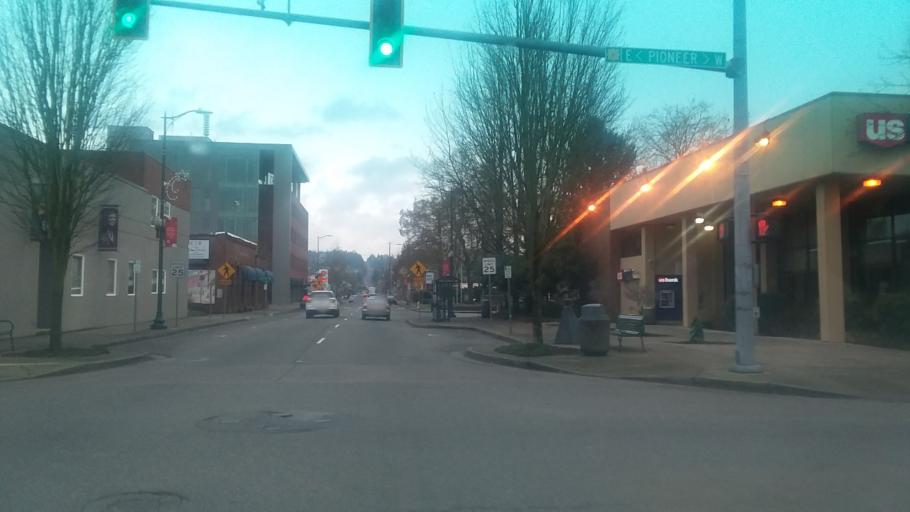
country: US
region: Washington
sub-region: Pierce County
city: Puyallup
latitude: 47.1905
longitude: -122.2938
